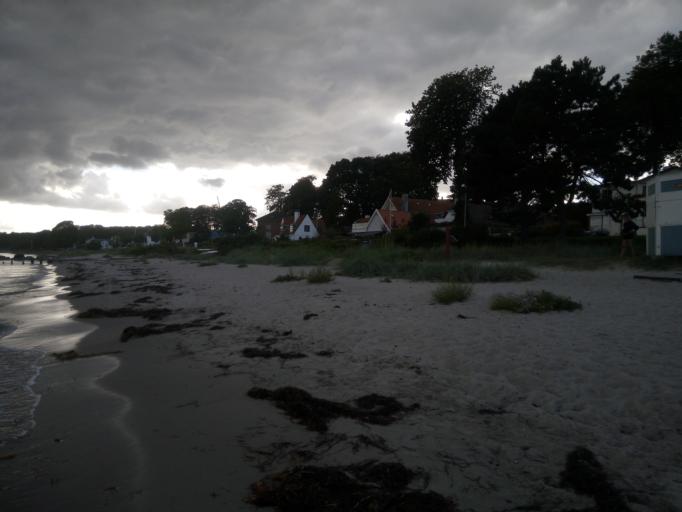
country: DK
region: Capital Region
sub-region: Helsingor Kommune
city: Espergaerde
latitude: 56.0076
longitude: 12.5863
